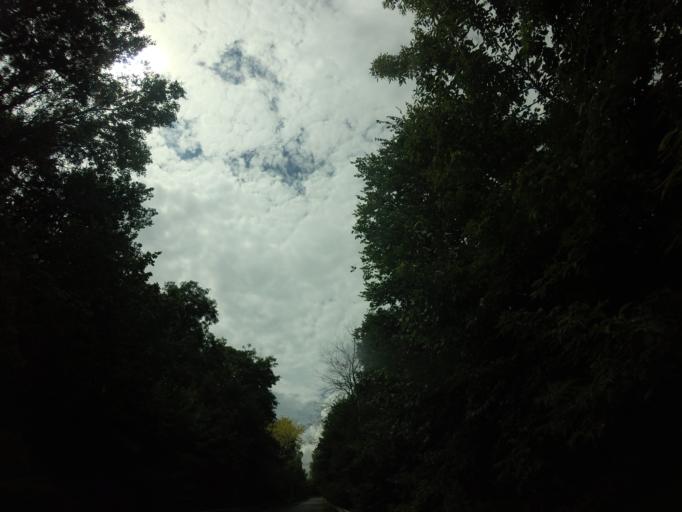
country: PL
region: Lublin Voivodeship
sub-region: Powiat opolski
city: Wilkow
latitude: 51.2737
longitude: 21.9253
